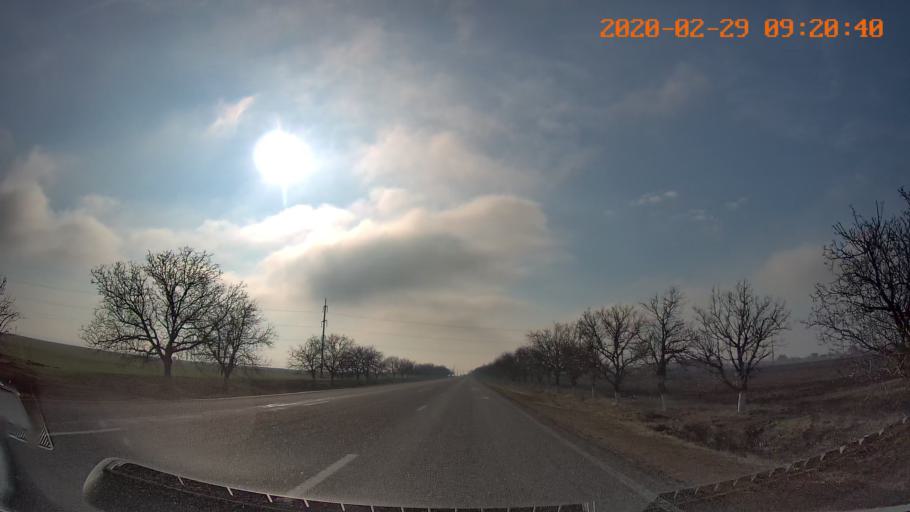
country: MD
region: Telenesti
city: Pervomaisc
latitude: 46.7457
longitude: 29.9511
